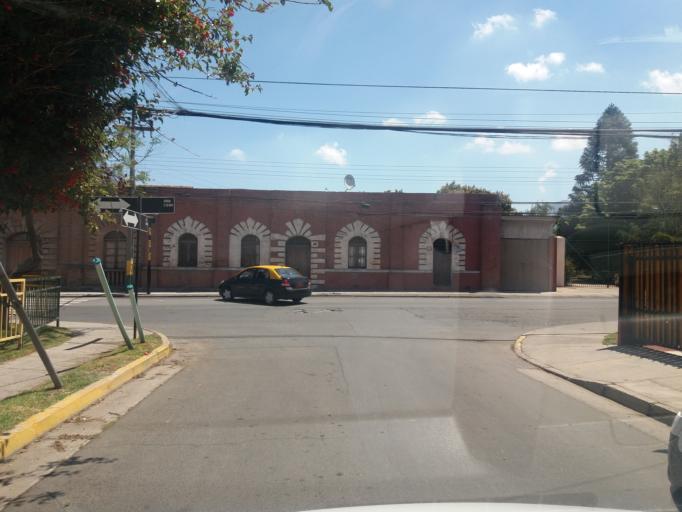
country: CL
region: Valparaiso
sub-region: Provincia de Quillota
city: Hacienda La Calera
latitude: -32.8228
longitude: -71.2260
